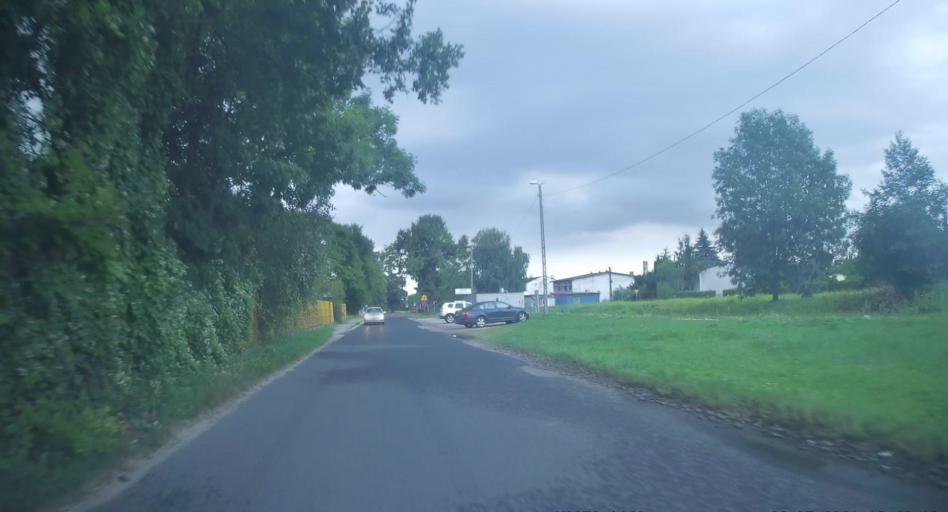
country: PL
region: Lodz Voivodeship
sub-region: Powiat brzezinski
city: Rogow
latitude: 51.8167
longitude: 19.8850
